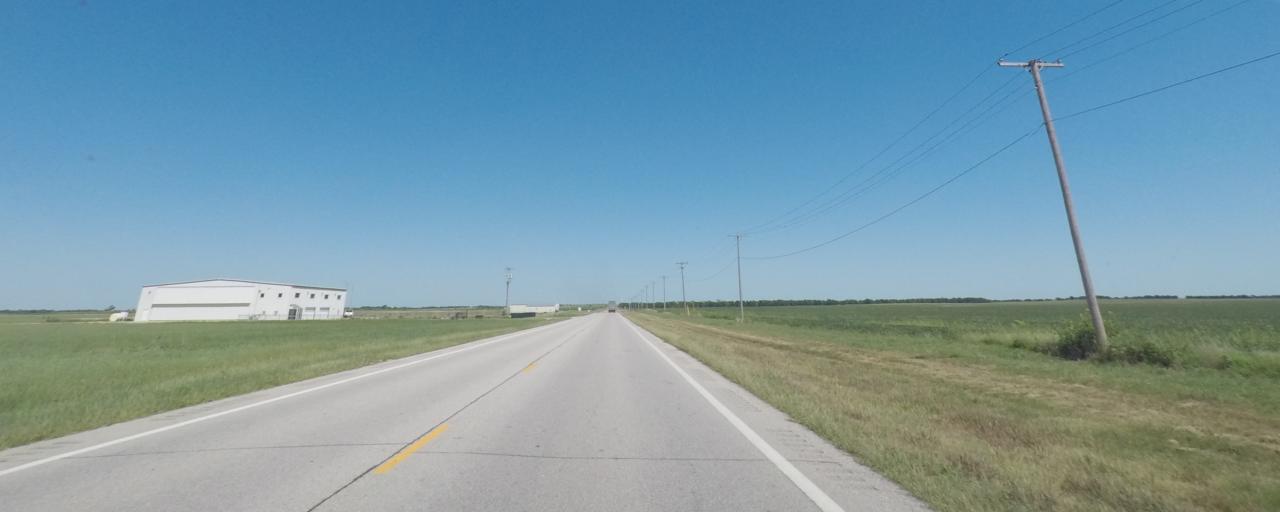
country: US
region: Kansas
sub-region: Sumner County
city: Wellington
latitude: 37.3272
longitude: -97.3848
